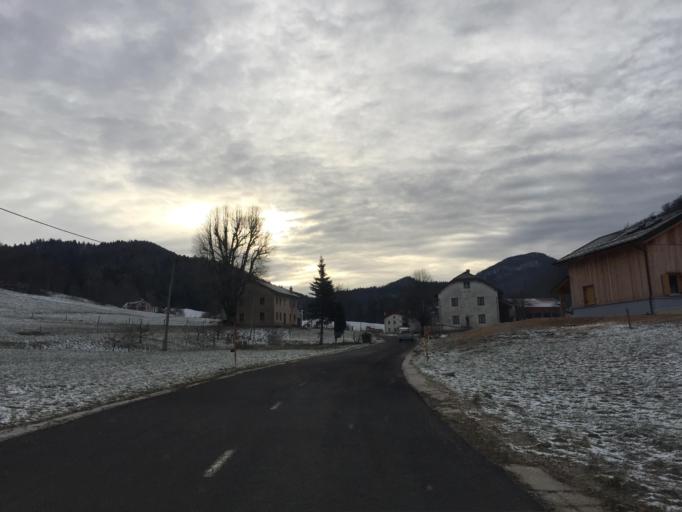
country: SI
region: Nova Gorica
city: Sempas
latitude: 46.0070
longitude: 13.7969
